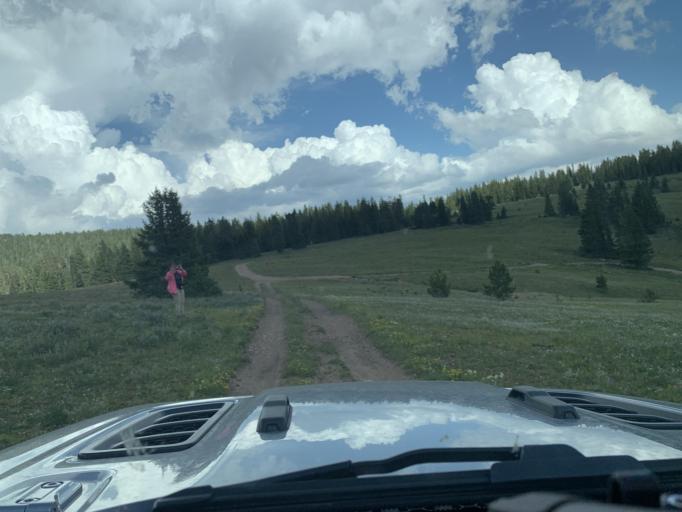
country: US
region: Colorado
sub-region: Lake County
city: Leadville North
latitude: 39.3075
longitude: -106.2881
